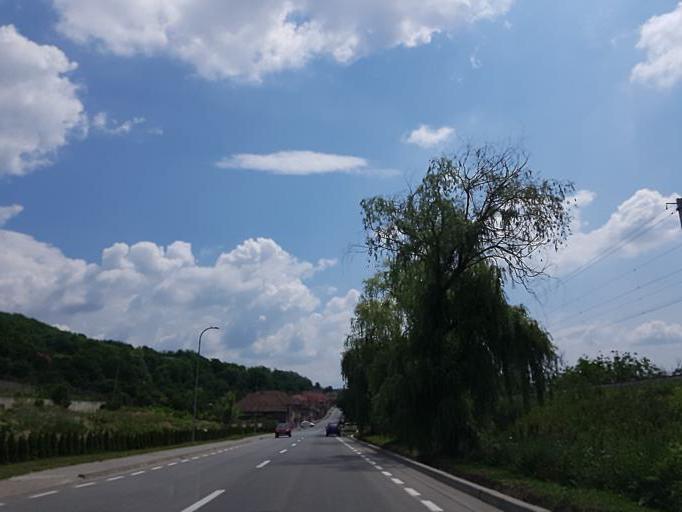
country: RO
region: Alba
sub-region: Municipiul Blaj
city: Veza
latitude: 46.1767
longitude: 23.9300
